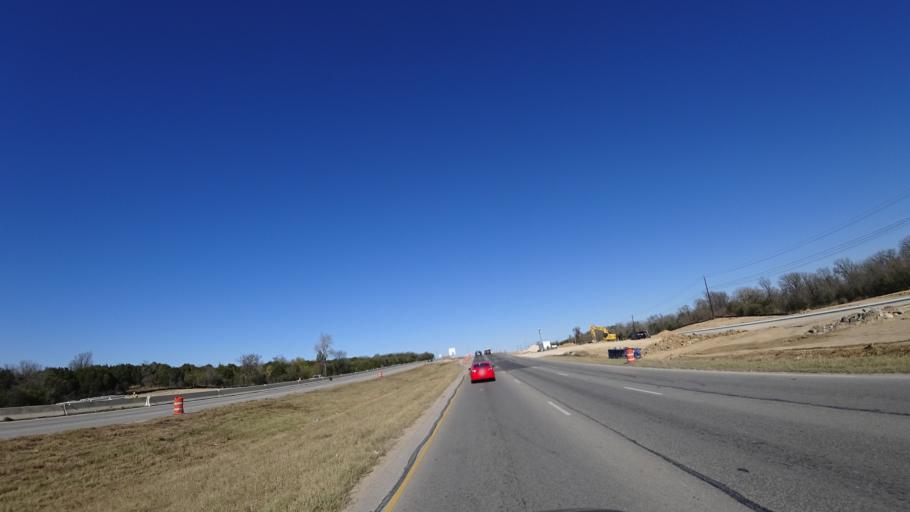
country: US
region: Texas
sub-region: Travis County
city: Austin
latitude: 30.2976
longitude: -97.6621
